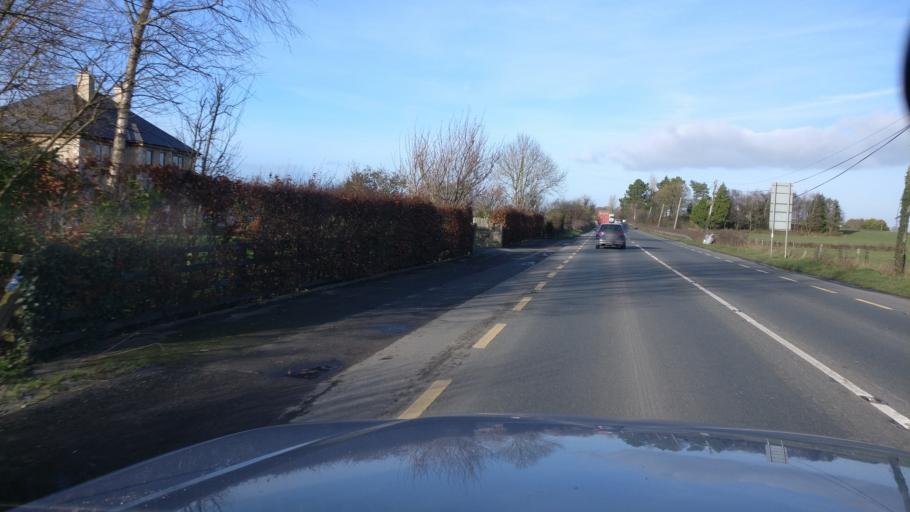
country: IE
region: Leinster
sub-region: Uibh Fhaili
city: Tullamore
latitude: 53.2426
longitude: -7.4779
